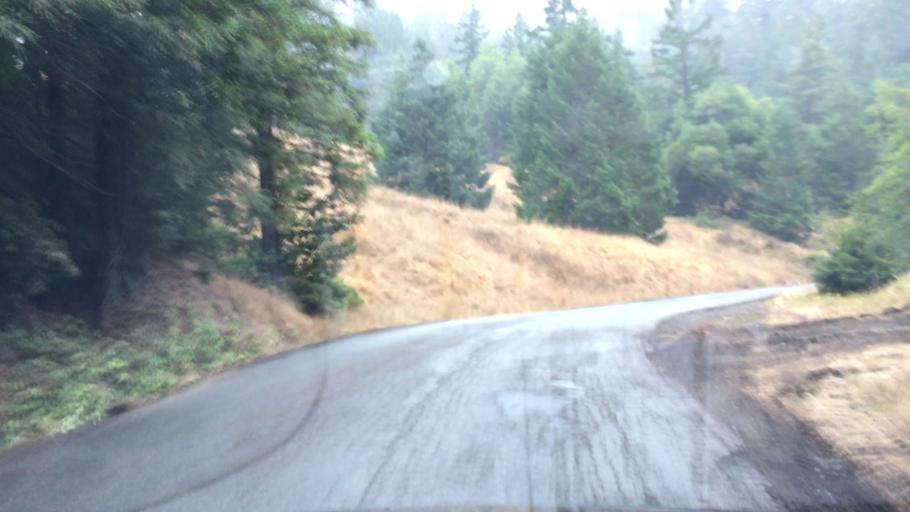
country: US
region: California
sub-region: Humboldt County
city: Rio Dell
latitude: 40.3526
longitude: -123.9861
